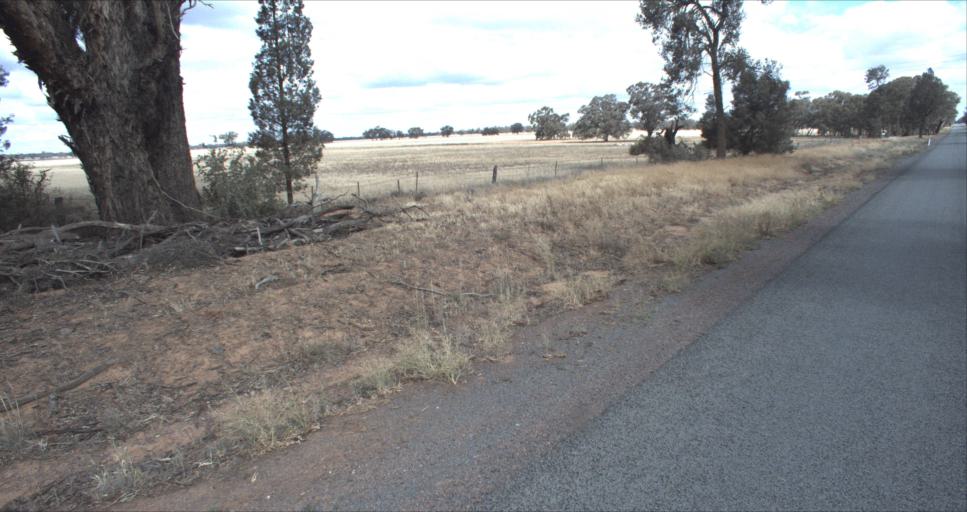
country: AU
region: New South Wales
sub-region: Leeton
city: Leeton
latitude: -34.6610
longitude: 146.3493
